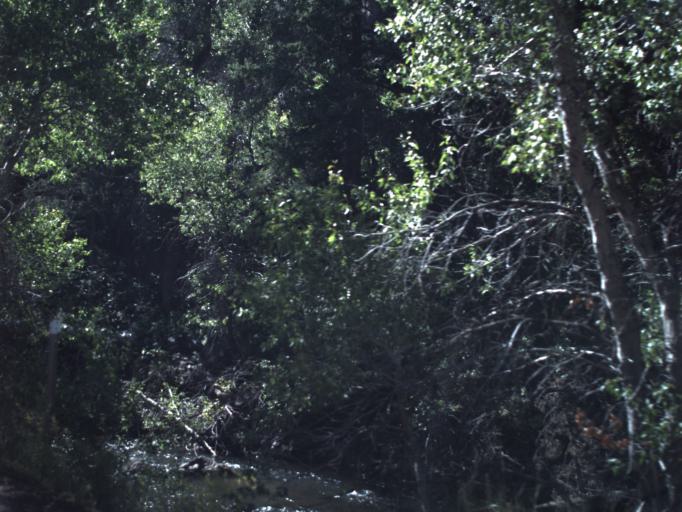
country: US
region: Utah
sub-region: Beaver County
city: Beaver
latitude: 38.2520
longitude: -112.5381
